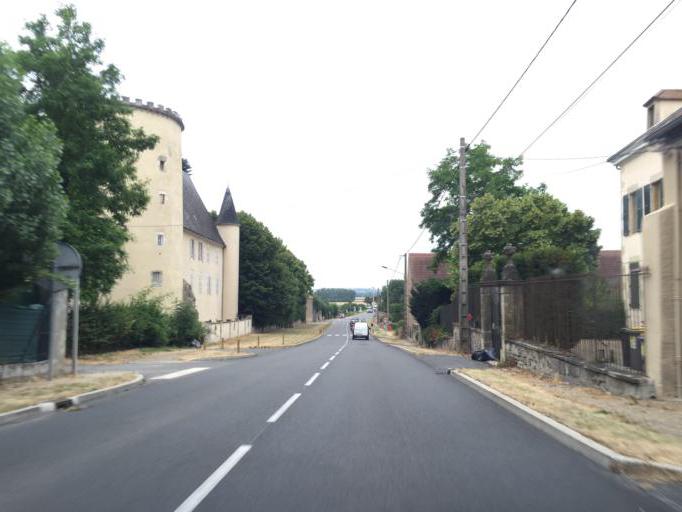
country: FR
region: Auvergne
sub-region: Departement de l'Allier
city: Brout-Vernet
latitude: 46.1643
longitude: 3.2374
